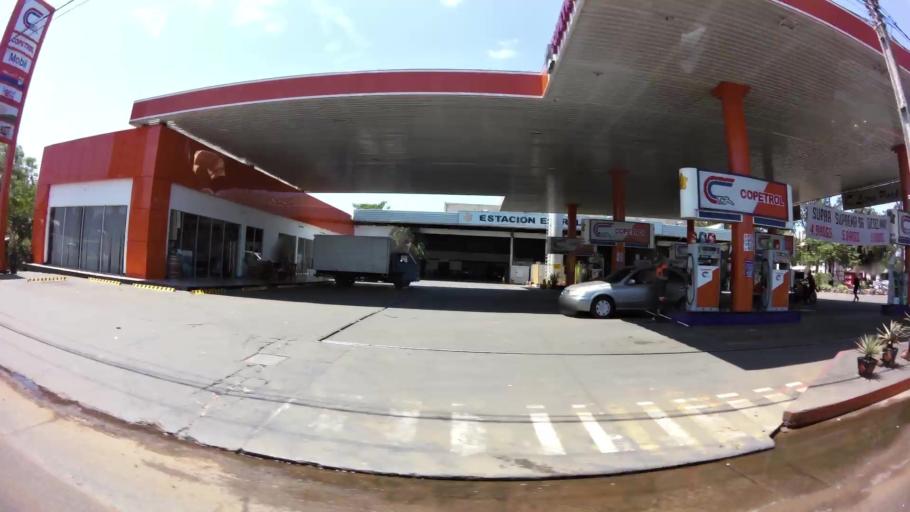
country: PY
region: Central
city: Nemby
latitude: -25.3881
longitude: -57.5479
